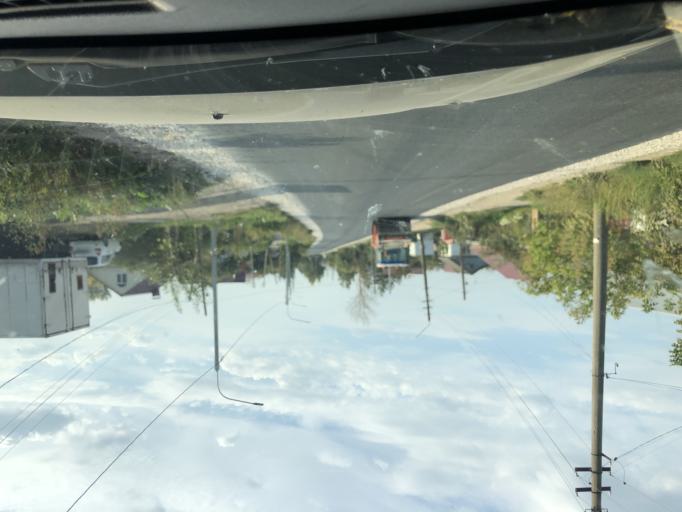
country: RU
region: Tula
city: Leninskiy
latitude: 54.2918
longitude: 37.4640
